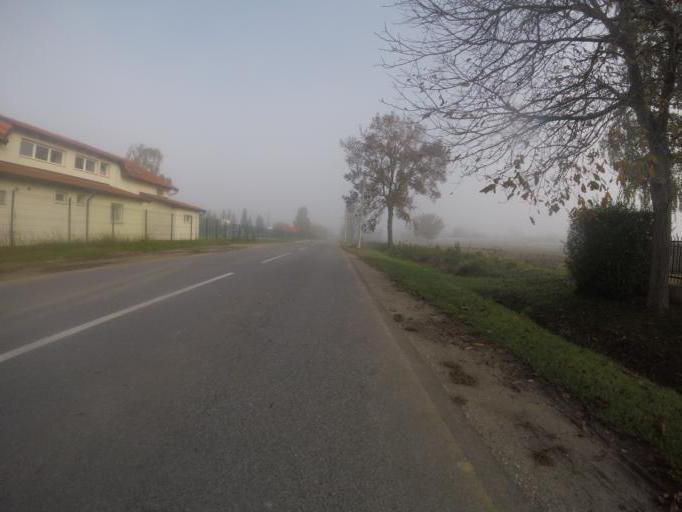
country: HR
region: Zagrebacka
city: Micevec
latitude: 45.7538
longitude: 16.0530
